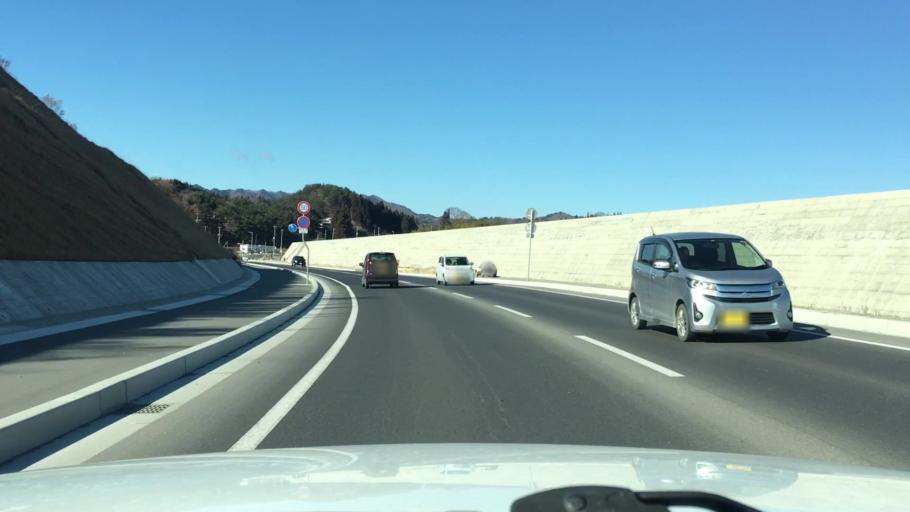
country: JP
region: Iwate
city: Yamada
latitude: 39.4544
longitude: 141.9602
